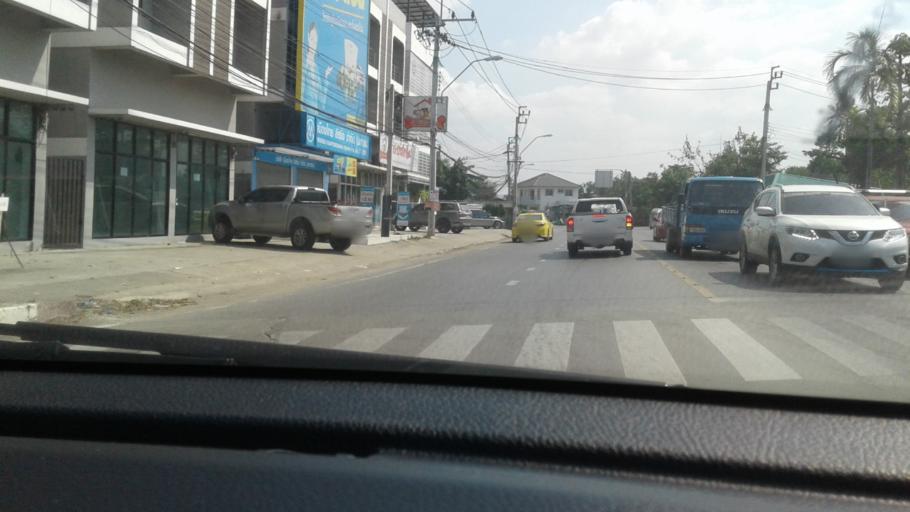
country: TH
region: Bangkok
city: Thawi Watthana
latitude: 13.7989
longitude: 100.3640
